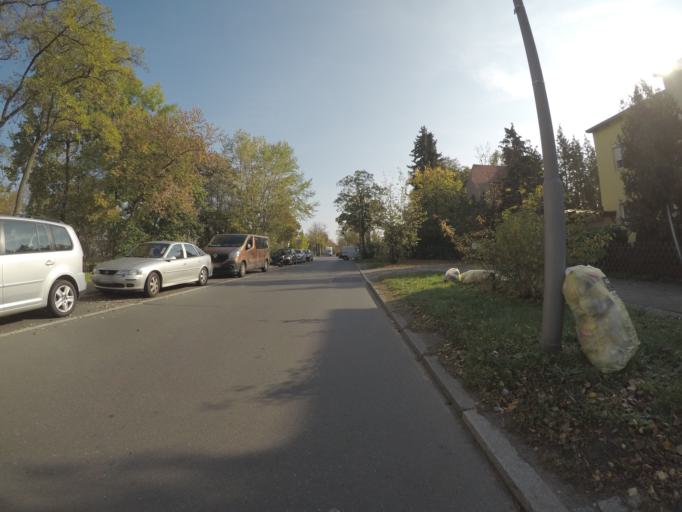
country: DE
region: Berlin
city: Rudow
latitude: 52.4321
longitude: 13.4943
